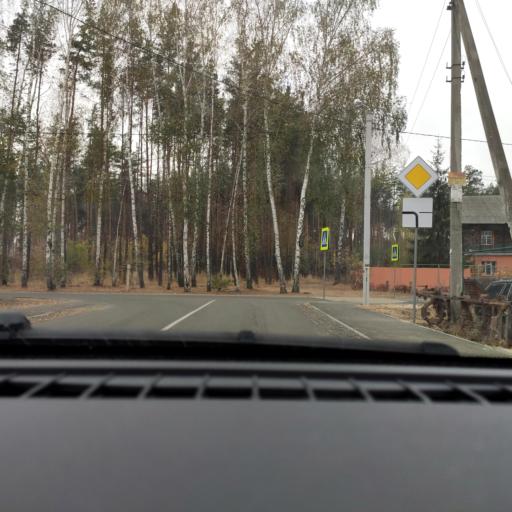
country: RU
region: Voronezj
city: Somovo
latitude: 51.7441
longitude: 39.3217
